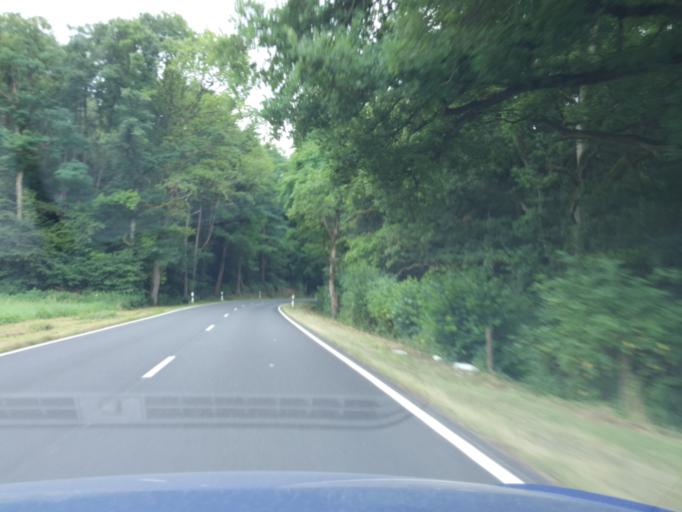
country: LU
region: Luxembourg
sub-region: Canton de Capellen
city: Kehlen
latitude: 49.6515
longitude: 6.0286
